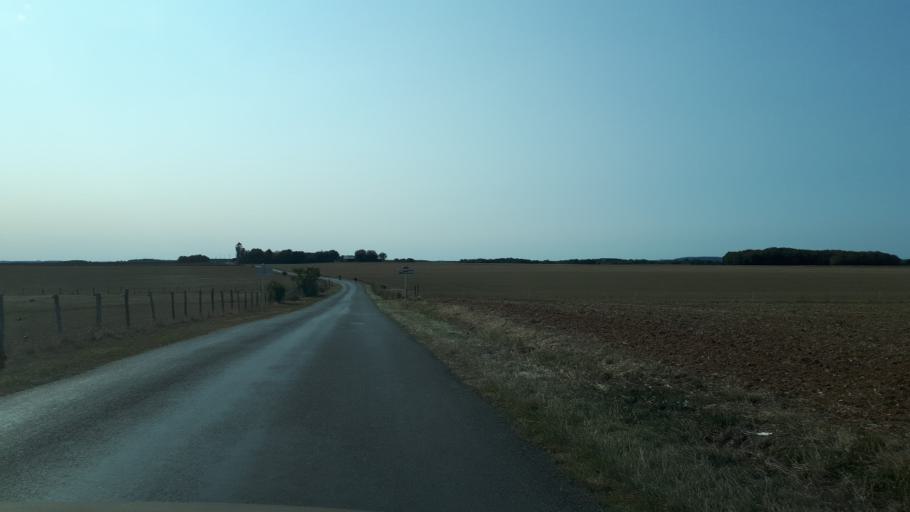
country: FR
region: Centre
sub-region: Departement du Cher
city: Rians
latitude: 47.1848
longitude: 2.7032
